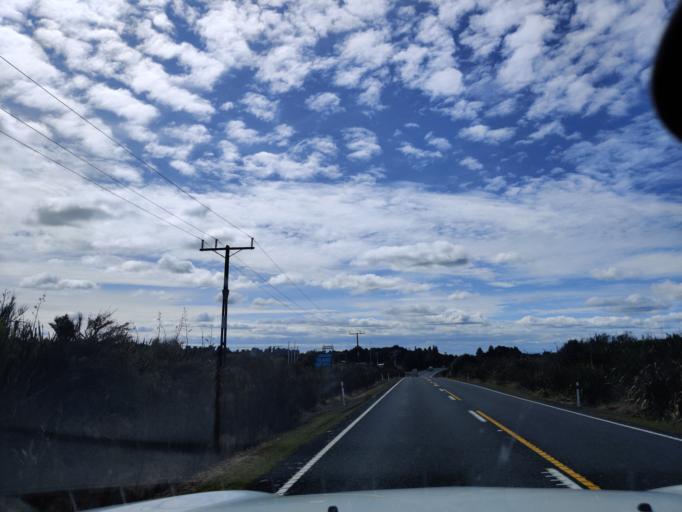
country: NZ
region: Manawatu-Wanganui
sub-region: Ruapehu District
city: Waiouru
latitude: -39.1607
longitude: 175.3997
